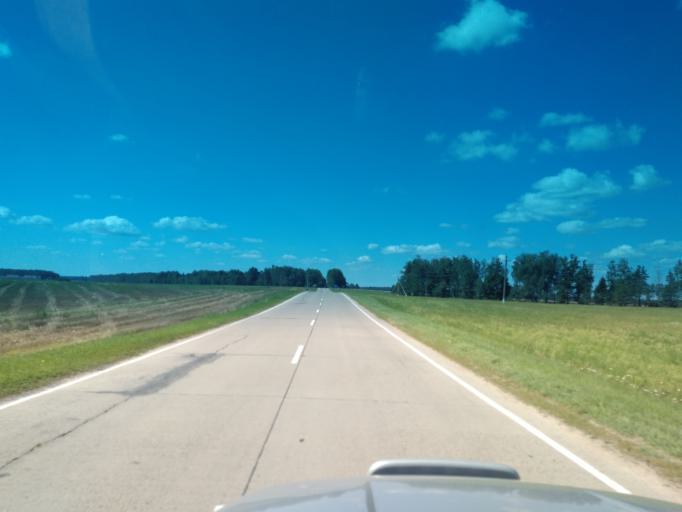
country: BY
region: Minsk
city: Stan'kava
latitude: 53.6262
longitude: 27.2643
